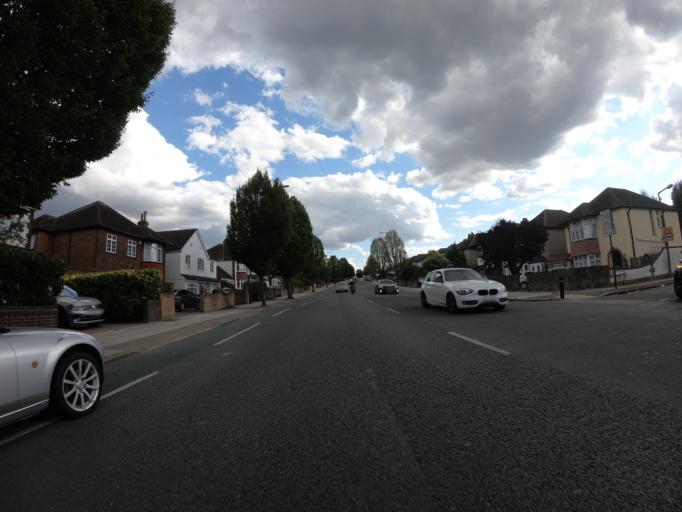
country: GB
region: England
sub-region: Greater London
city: Chislehurst
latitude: 51.4289
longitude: 0.0642
